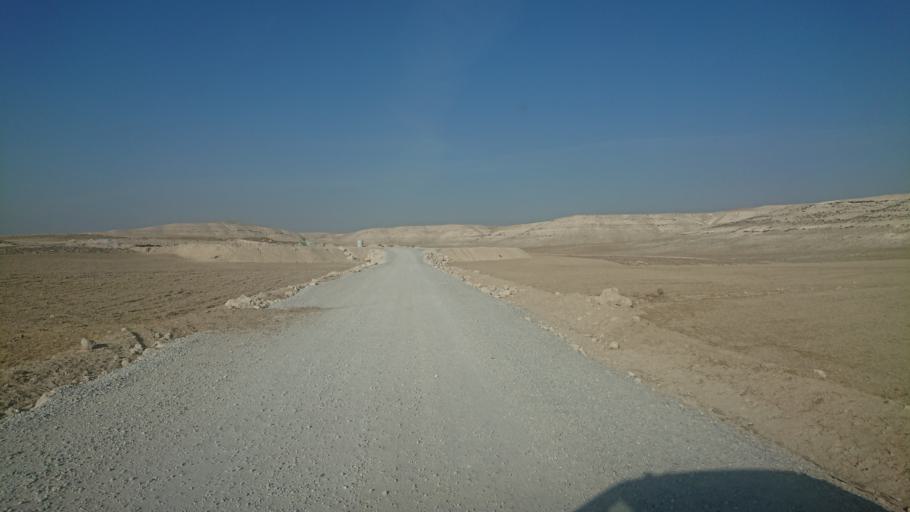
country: TR
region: Aksaray
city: Sultanhani
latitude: 38.0843
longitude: 33.6209
